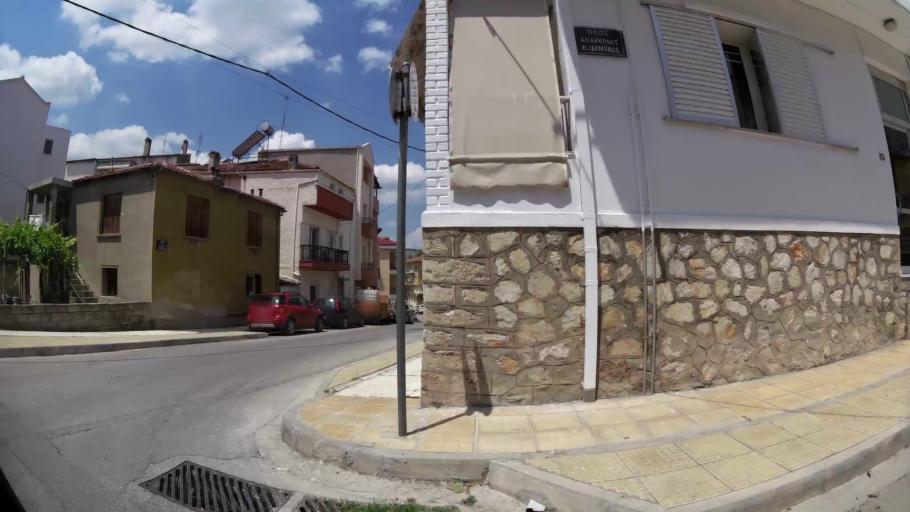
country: GR
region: West Macedonia
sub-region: Nomos Kozanis
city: Kozani
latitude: 40.2966
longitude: 21.7958
